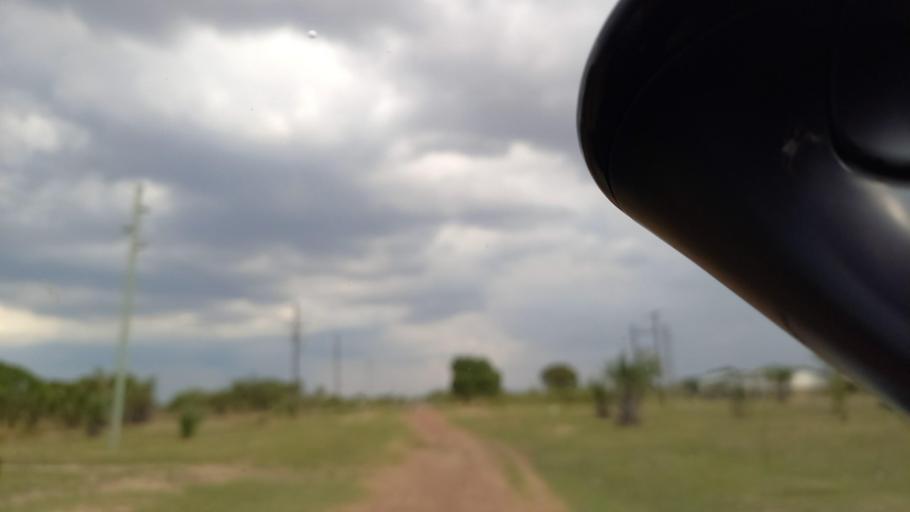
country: ZM
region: Lusaka
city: Kafue
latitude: -15.8494
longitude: 28.1079
